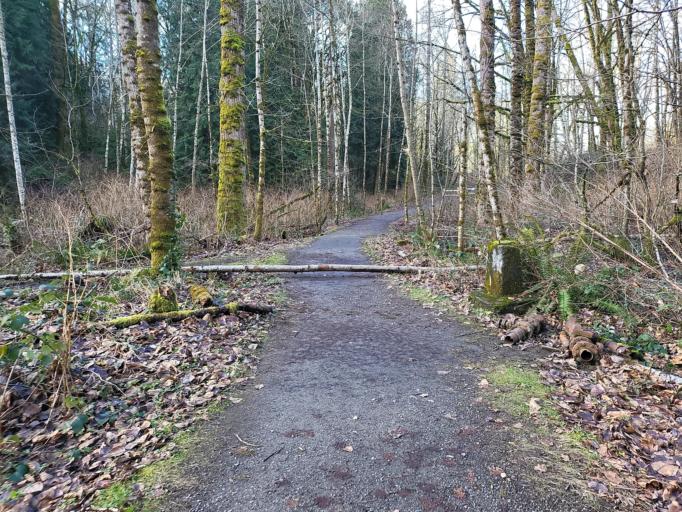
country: US
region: Washington
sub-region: King County
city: Newcastle
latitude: 47.5327
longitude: -122.1278
